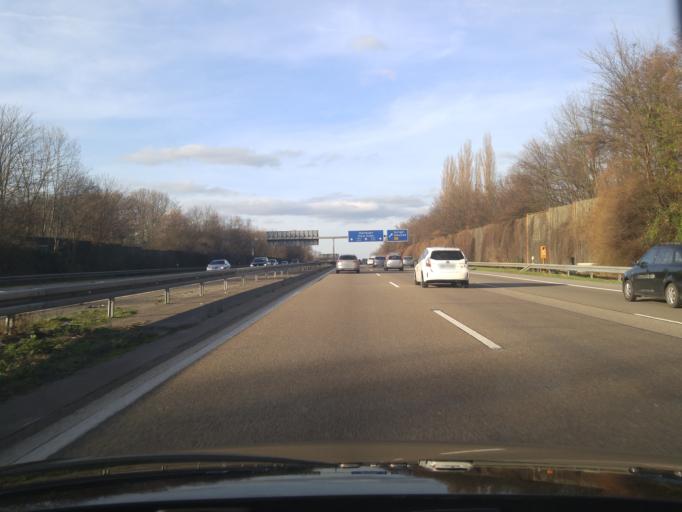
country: DE
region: North Rhine-Westphalia
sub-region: Regierungsbezirk Dusseldorf
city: Langenfeld
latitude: 51.1198
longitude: 6.9823
